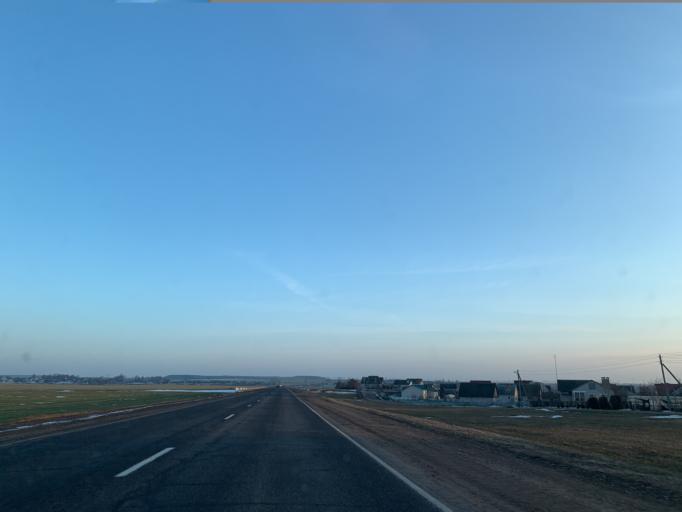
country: BY
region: Minsk
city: Haradzyeya
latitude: 53.3135
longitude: 26.5645
